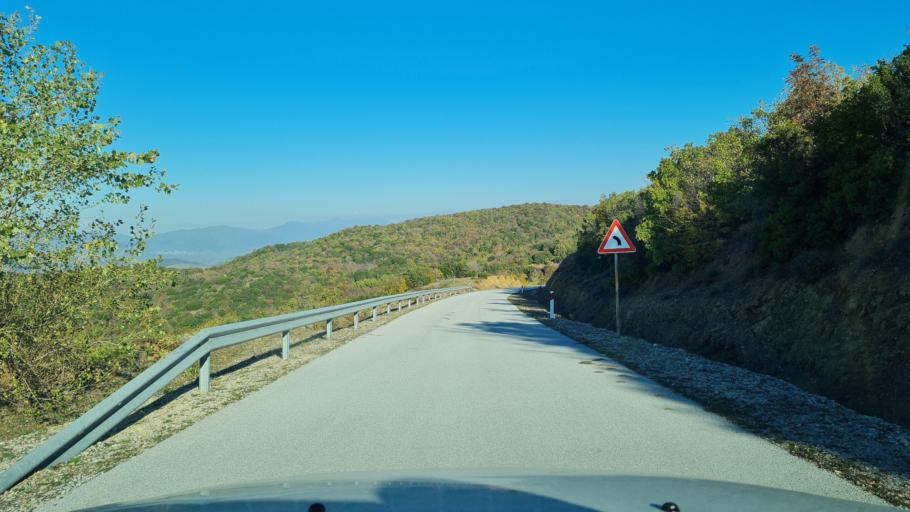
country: MK
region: Bogdanci
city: Bogdanci
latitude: 41.2254
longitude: 22.5541
